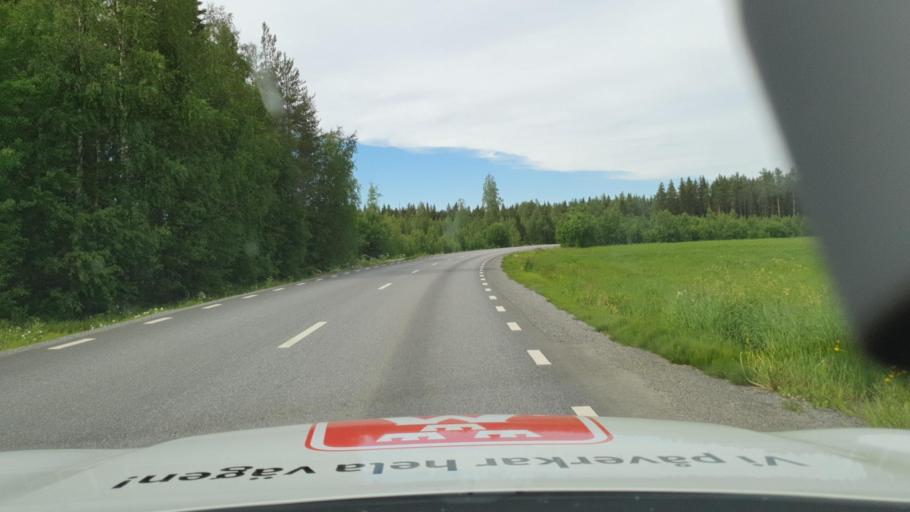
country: SE
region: Vaesterbotten
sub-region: Skelleftea Kommun
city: Burtraesk
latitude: 64.5001
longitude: 20.6259
